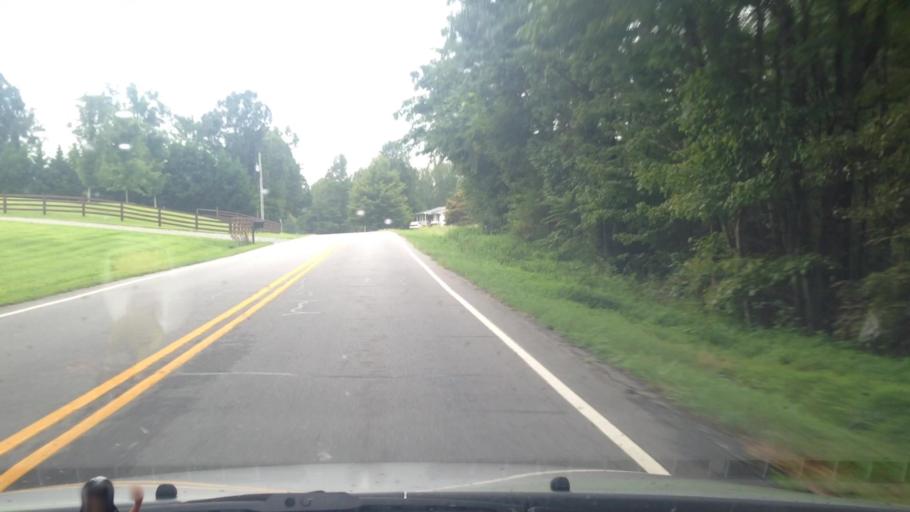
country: US
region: North Carolina
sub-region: Stokes County
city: Danbury
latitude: 36.4254
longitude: -80.1082
